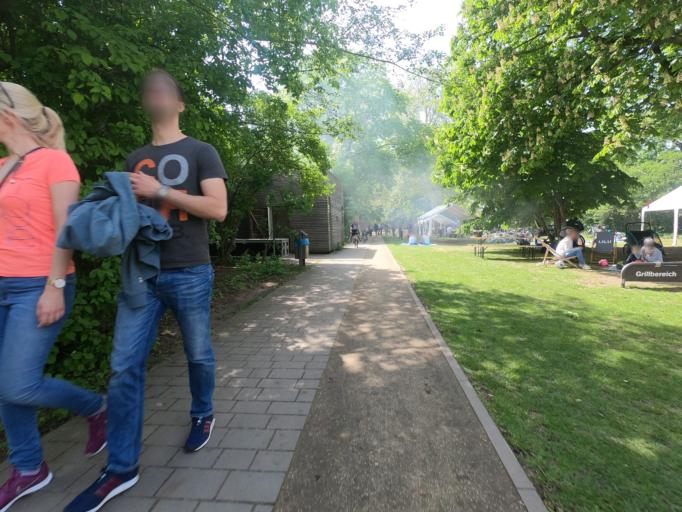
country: DE
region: Hesse
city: Niederrad
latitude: 50.0934
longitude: 8.6457
